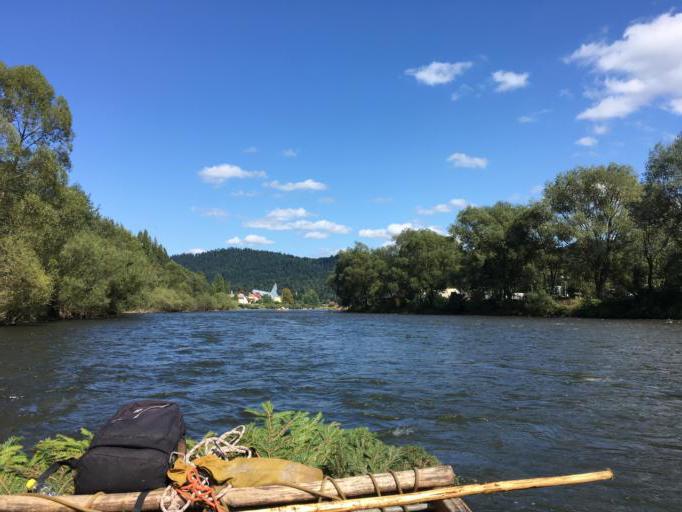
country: PL
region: Lesser Poland Voivodeship
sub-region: Powiat nowotarski
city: Kroscienko nad Dunajcem
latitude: 49.3905
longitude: 20.3952
